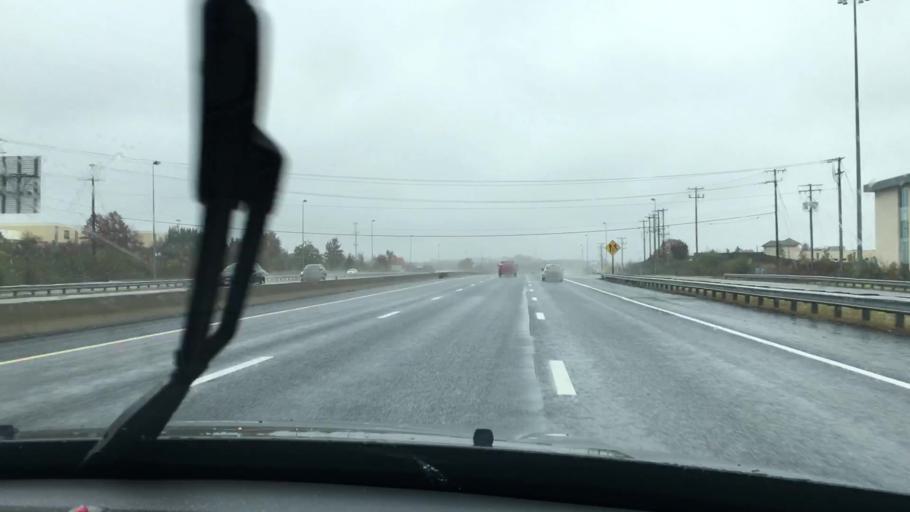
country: US
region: Virginia
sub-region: Loudoun County
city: Sterling
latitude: 39.0250
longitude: -77.4316
